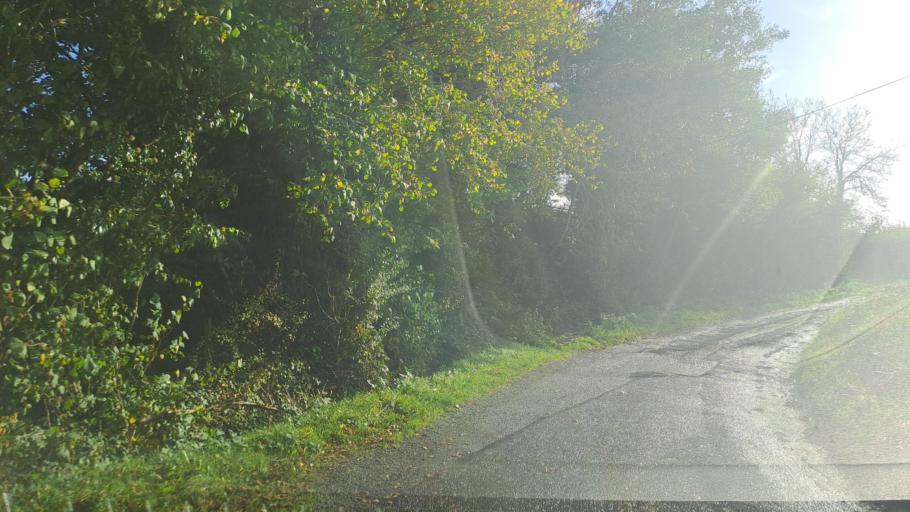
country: IE
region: Ulster
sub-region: An Cabhan
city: Cootehill
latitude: 54.0100
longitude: -7.0393
